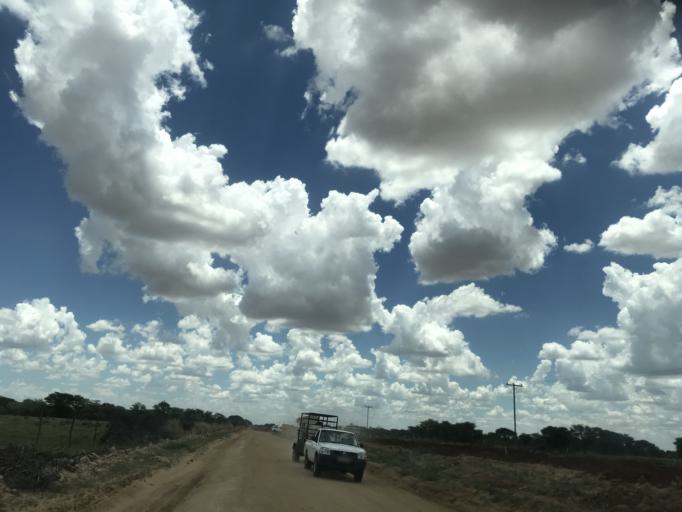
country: BW
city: Mabuli
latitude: -25.7901
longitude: 24.6467
